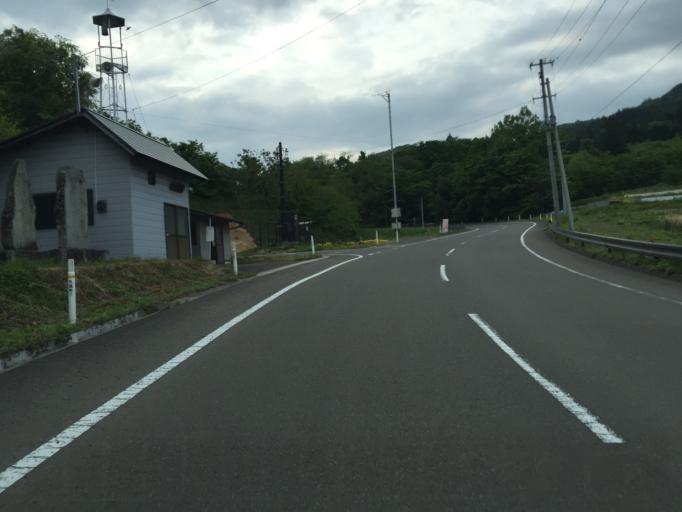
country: JP
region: Miyagi
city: Marumori
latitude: 37.9058
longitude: 140.6902
